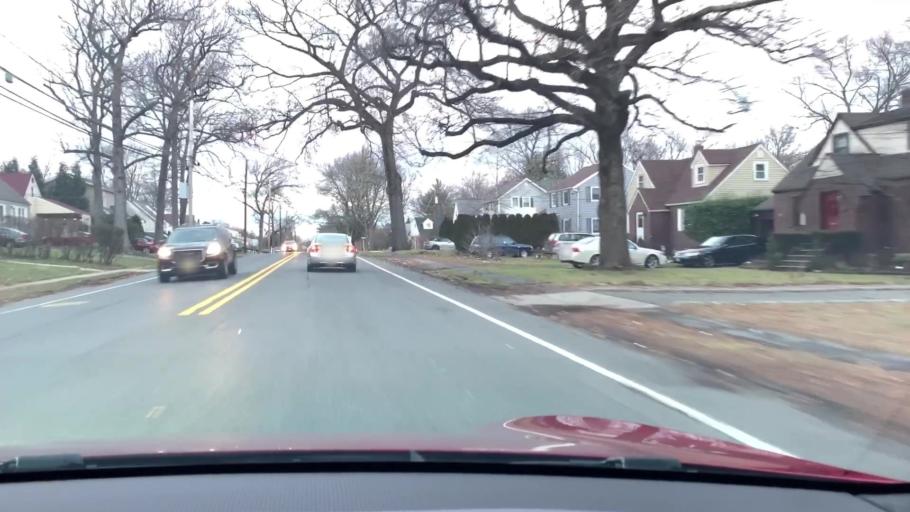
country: US
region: New Jersey
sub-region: Bergen County
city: Cresskill
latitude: 40.9444
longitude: -73.9765
